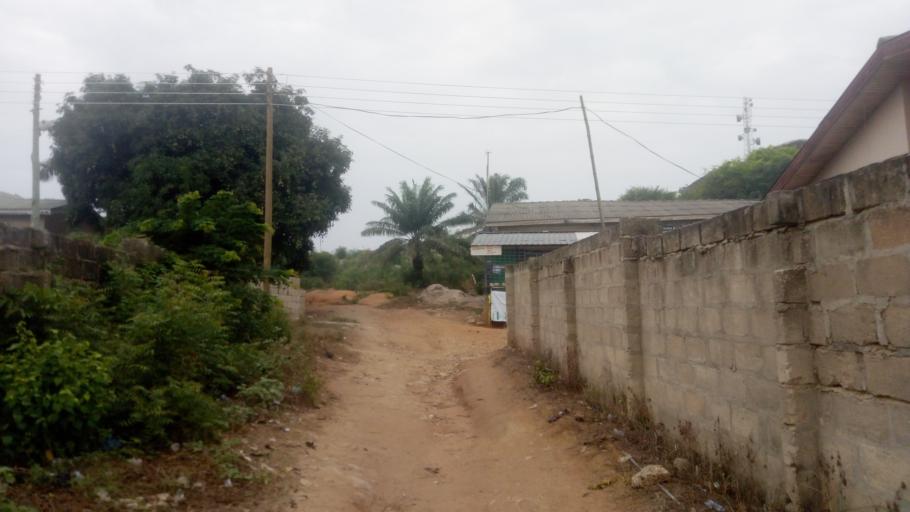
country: GH
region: Central
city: Winneba
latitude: 5.3572
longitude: -0.6259
